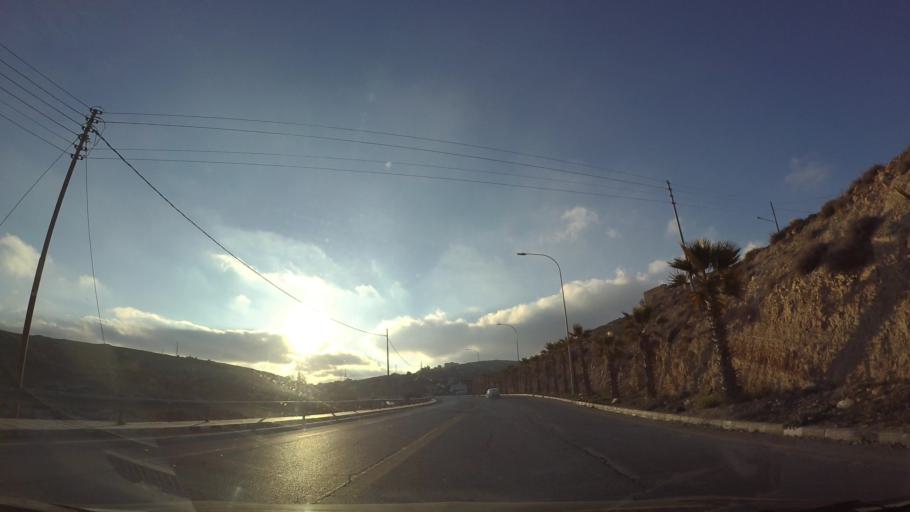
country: JO
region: Ma'an
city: Petra
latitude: 30.5213
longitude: 35.5529
